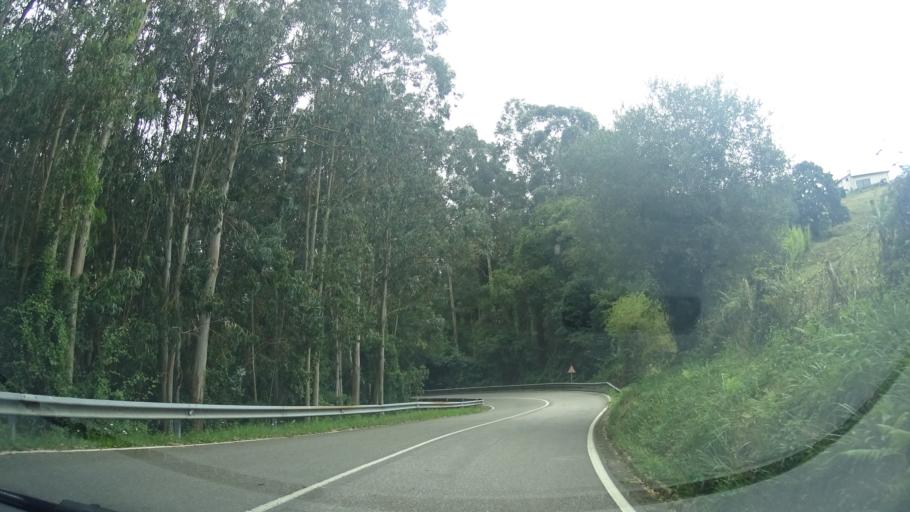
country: ES
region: Asturias
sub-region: Province of Asturias
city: Ribadesella
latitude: 43.4636
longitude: -5.0918
